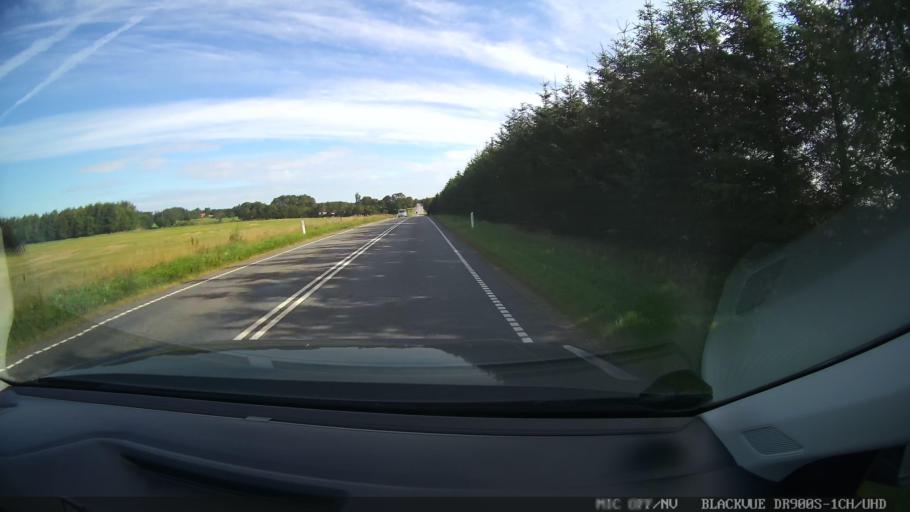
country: DK
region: North Denmark
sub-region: Rebild Kommune
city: Skorping
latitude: 56.7748
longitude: 10.0023
